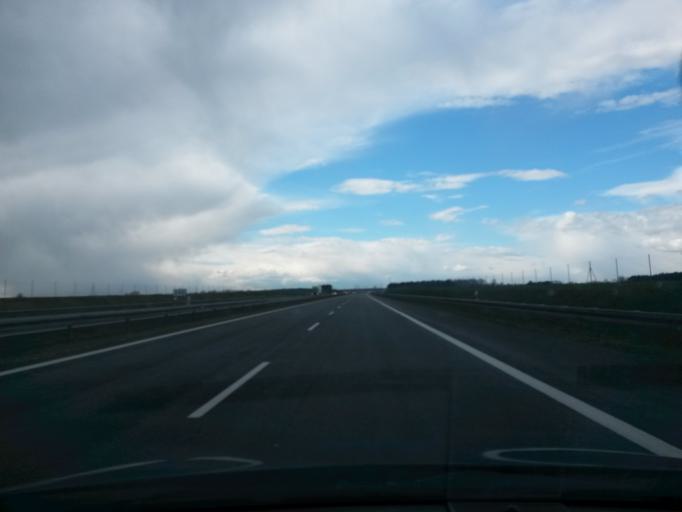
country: PL
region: Greater Poland Voivodeship
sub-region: Powiat slupecki
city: Ladek
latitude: 52.2163
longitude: 17.9715
